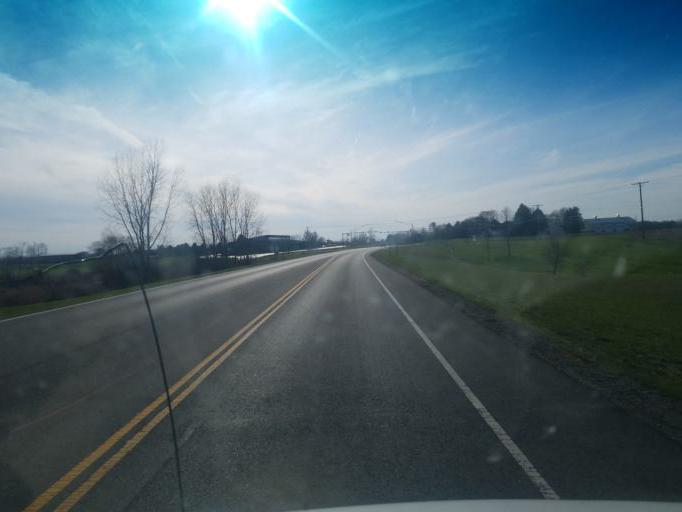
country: US
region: Ohio
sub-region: Logan County
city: Bellefontaine
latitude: 40.3626
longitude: -83.7896
